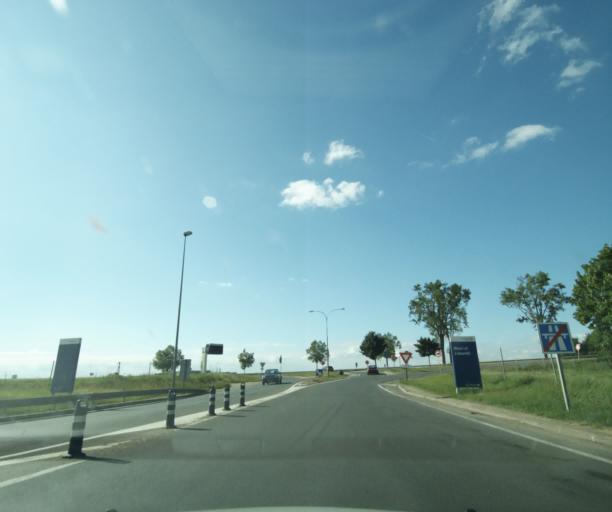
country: FR
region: Centre
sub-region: Departement d'Eure-et-Loir
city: Janville
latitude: 48.2059
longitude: 1.8455
